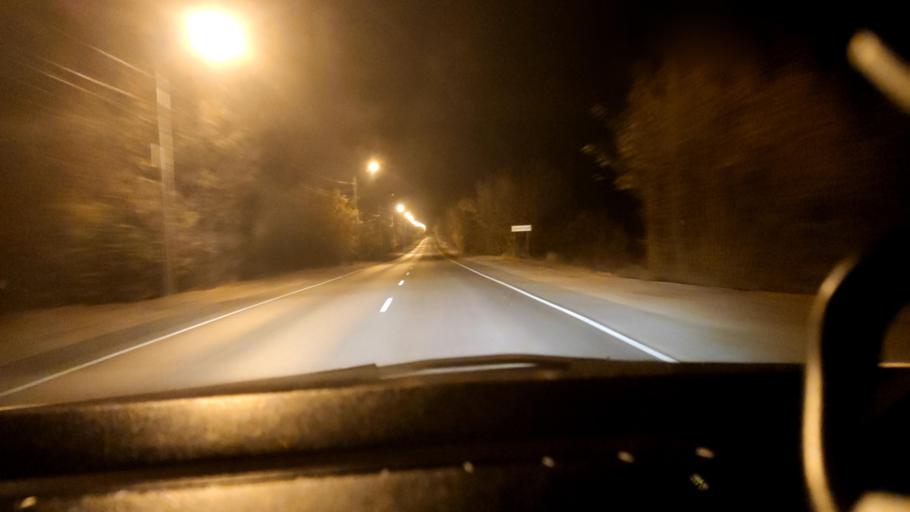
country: RU
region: Voronezj
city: Pridonskoy
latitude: 51.6376
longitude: 39.0874
